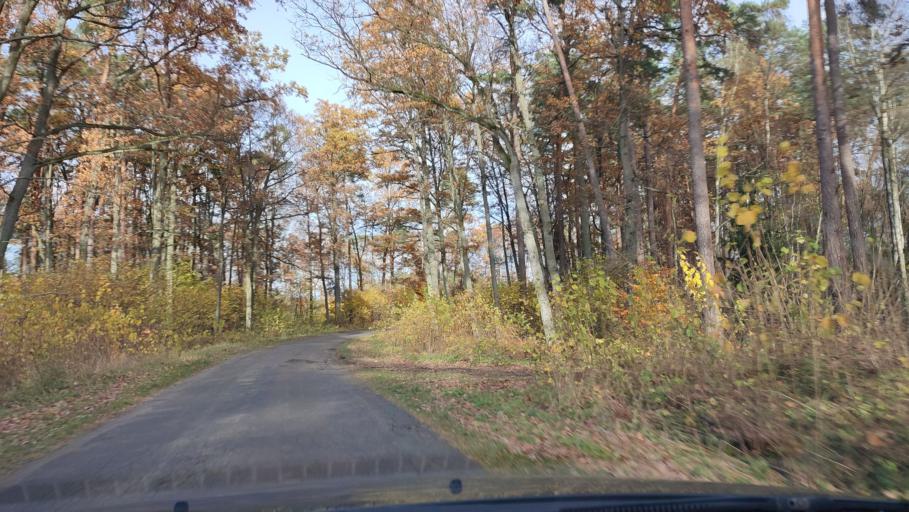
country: PL
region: Warmian-Masurian Voivodeship
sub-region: Powiat szczycienski
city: Szczytno
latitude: 53.5297
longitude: 20.9238
